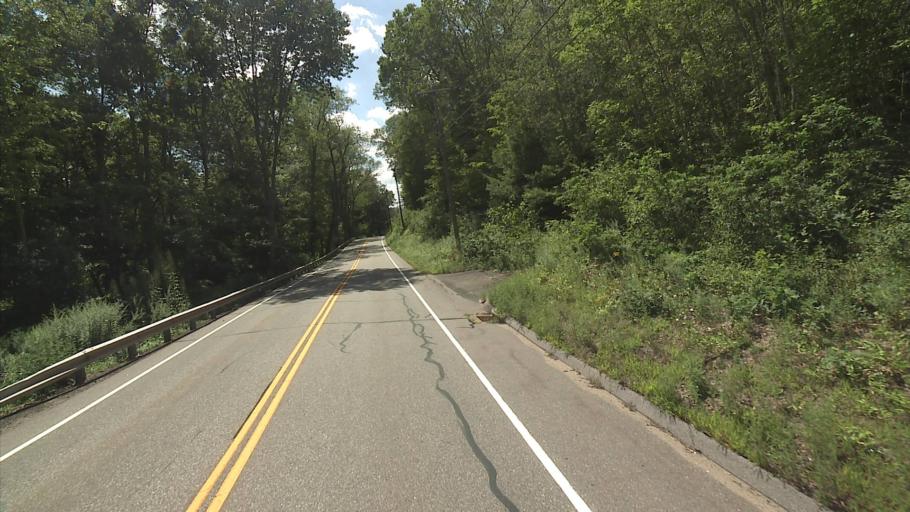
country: US
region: Connecticut
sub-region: Windham County
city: South Woodstock
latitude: 41.8957
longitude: -72.0790
